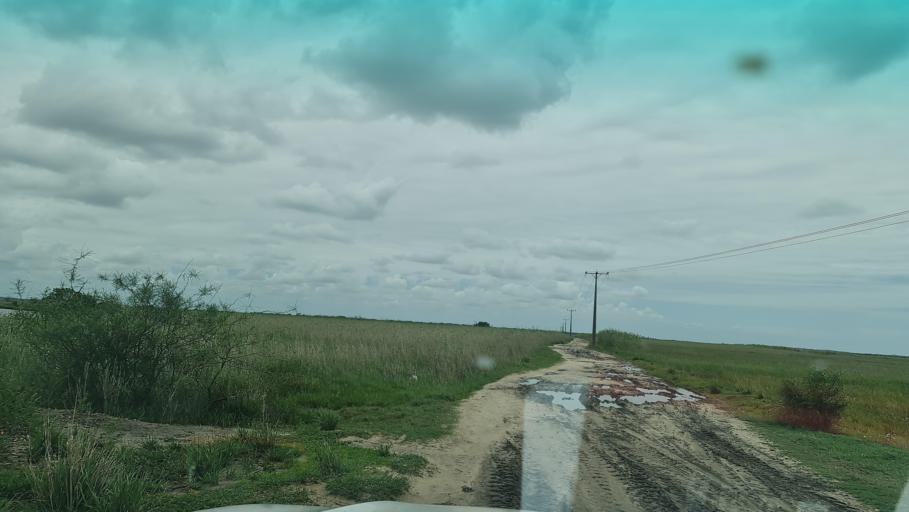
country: MZ
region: Maputo City
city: Maputo
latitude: -25.7215
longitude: 32.6991
